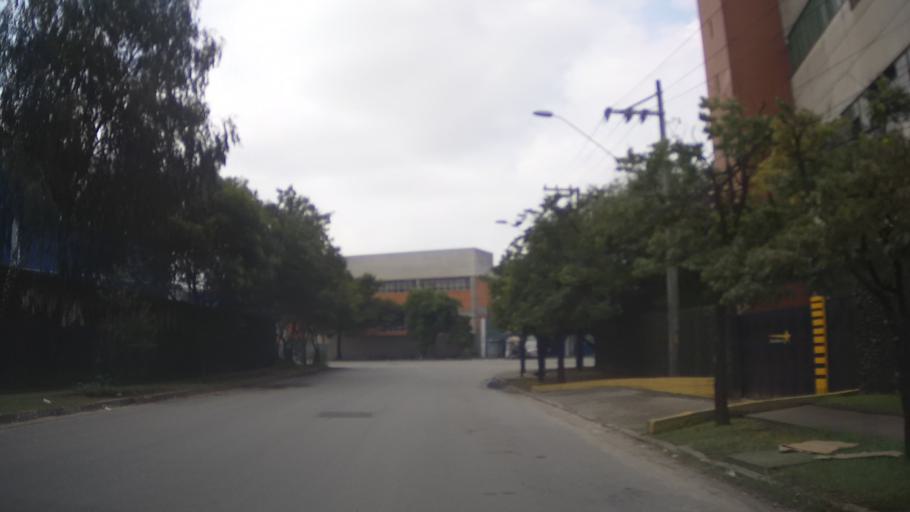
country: BR
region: Sao Paulo
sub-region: Guarulhos
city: Guarulhos
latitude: -23.4722
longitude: -46.4685
